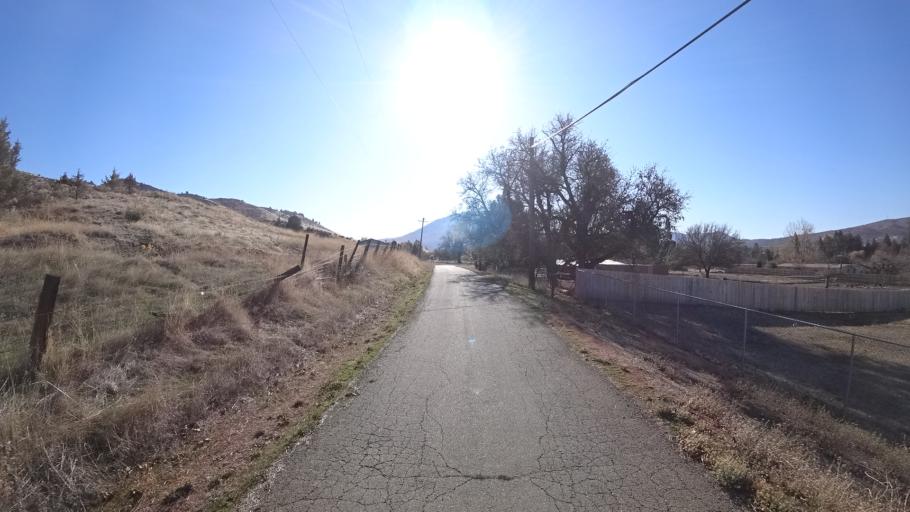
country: US
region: California
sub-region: Siskiyou County
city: Montague
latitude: 41.9147
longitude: -122.5578
